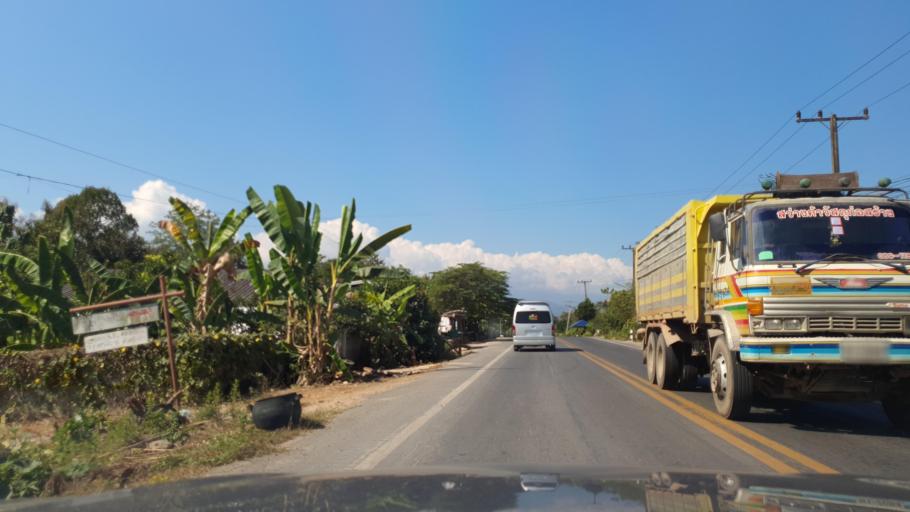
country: TH
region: Nan
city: Tha Wang Pha
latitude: 19.1040
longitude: 100.8200
